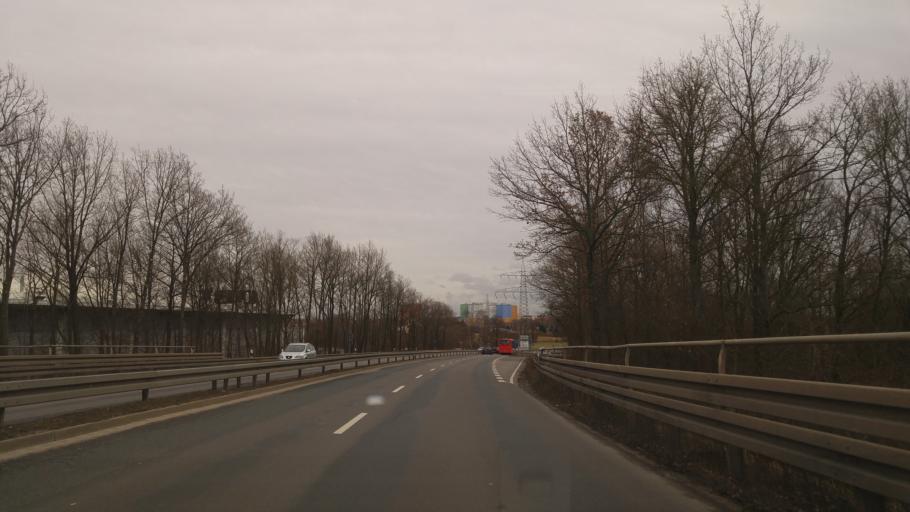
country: DE
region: Bavaria
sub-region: Regierungsbezirk Mittelfranken
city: Erlangen
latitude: 49.5866
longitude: 10.9743
